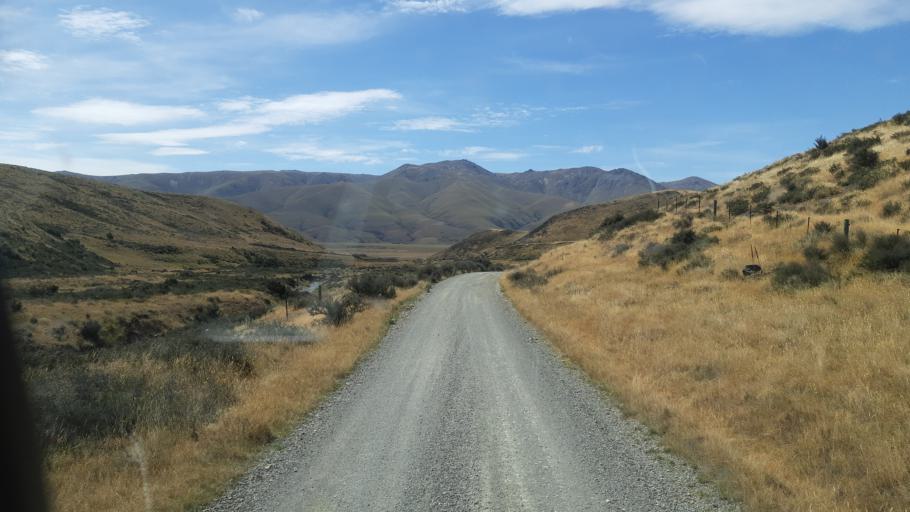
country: NZ
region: Canterbury
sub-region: Timaru District
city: Pleasant Point
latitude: -44.3532
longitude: 170.6085
